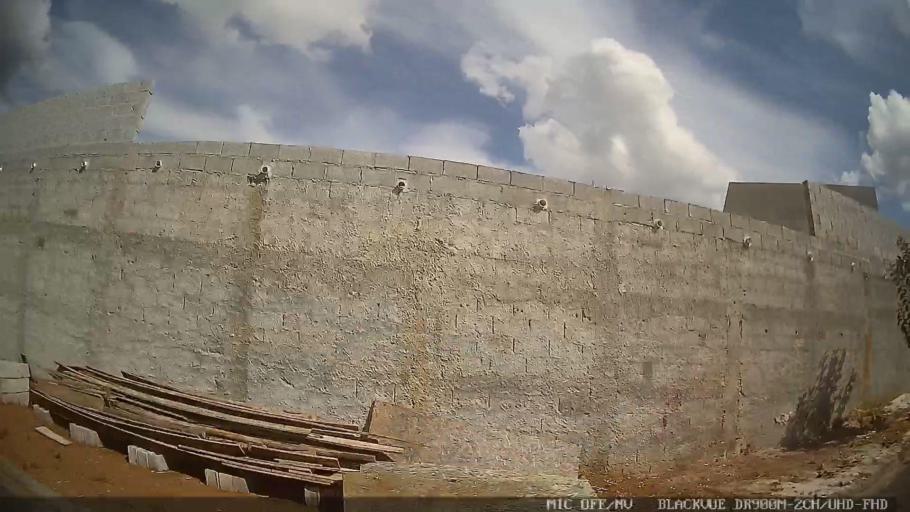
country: BR
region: Sao Paulo
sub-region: Atibaia
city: Atibaia
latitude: -23.0736
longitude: -46.5749
